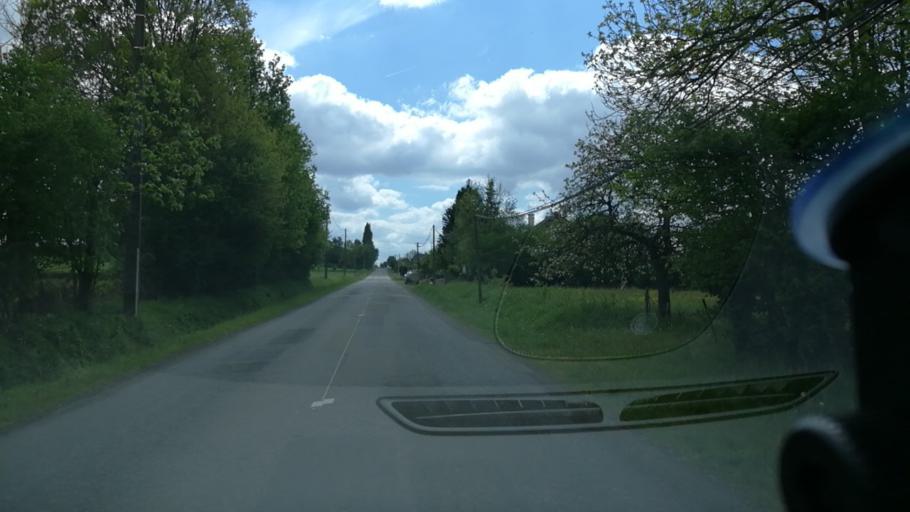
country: FR
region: Brittany
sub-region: Departement d'Ille-et-Vilaine
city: Retiers
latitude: 47.9059
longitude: -1.3802
